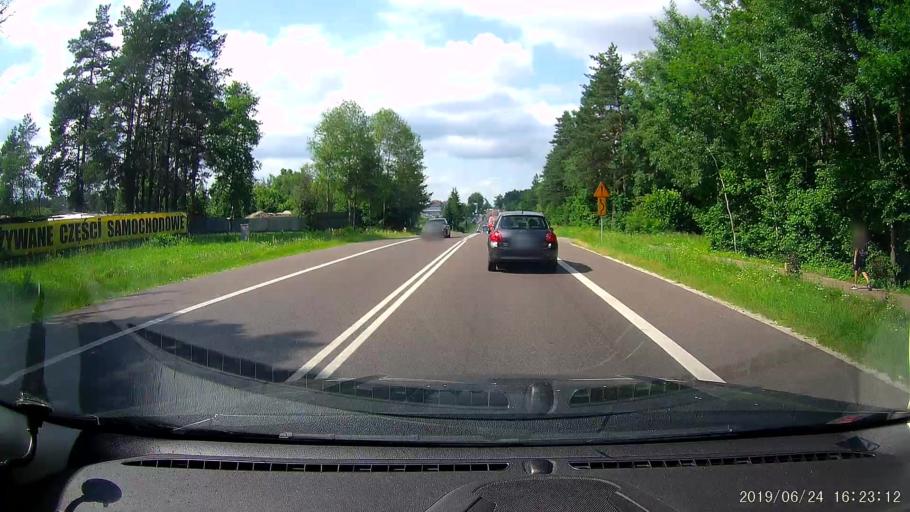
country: PL
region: Lublin Voivodeship
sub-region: Powiat tomaszowski
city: Tomaszow Lubelski
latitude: 50.4293
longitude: 23.4224
